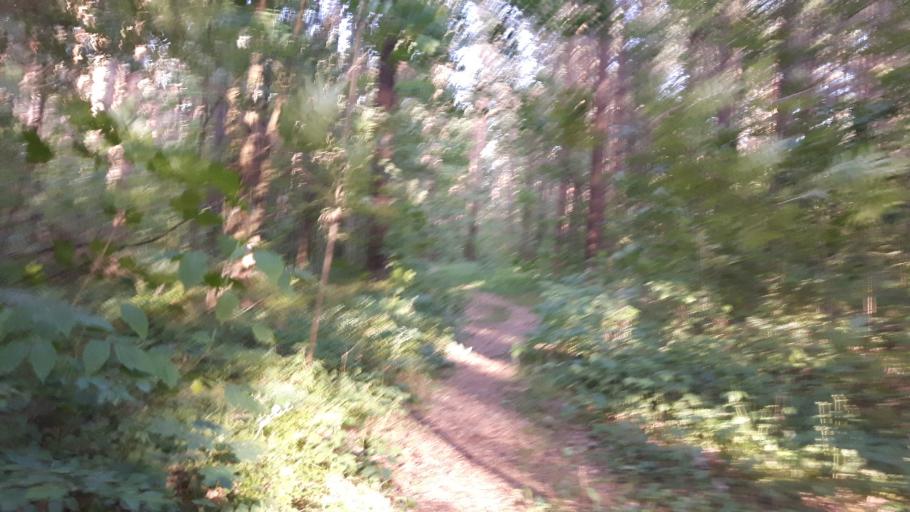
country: LV
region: Riga
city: Jaunciems
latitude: 57.0114
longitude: 24.1355
